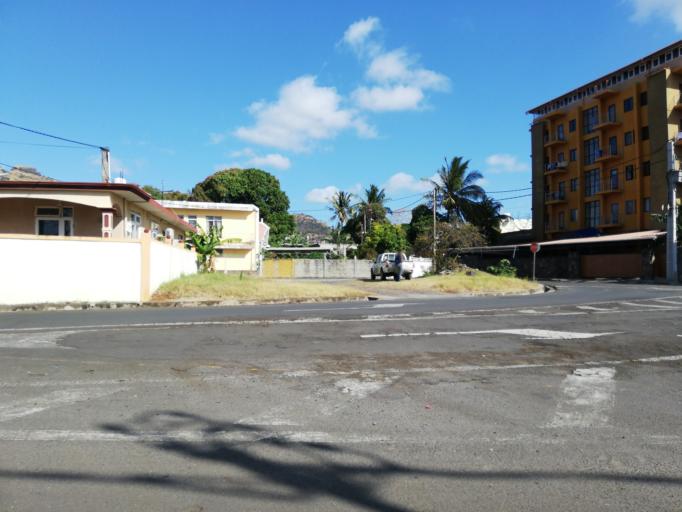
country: MU
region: Port Louis
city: Port Louis
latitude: -20.1643
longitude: 57.4800
